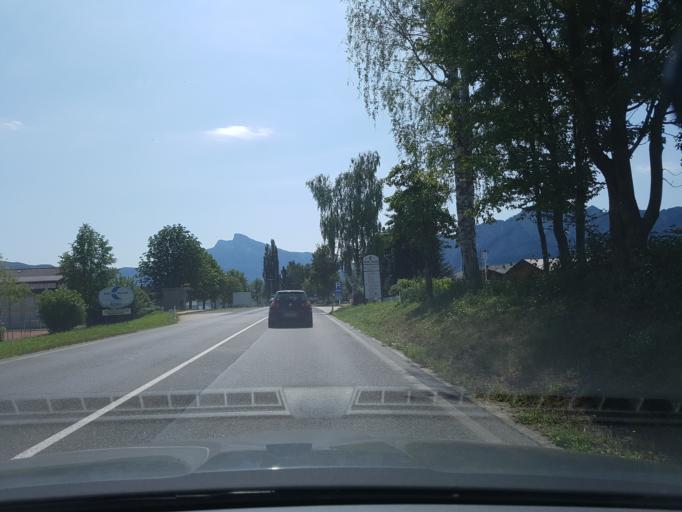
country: AT
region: Upper Austria
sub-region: Politischer Bezirk Vocklabruck
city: Mondsee
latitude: 47.8588
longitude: 13.3413
